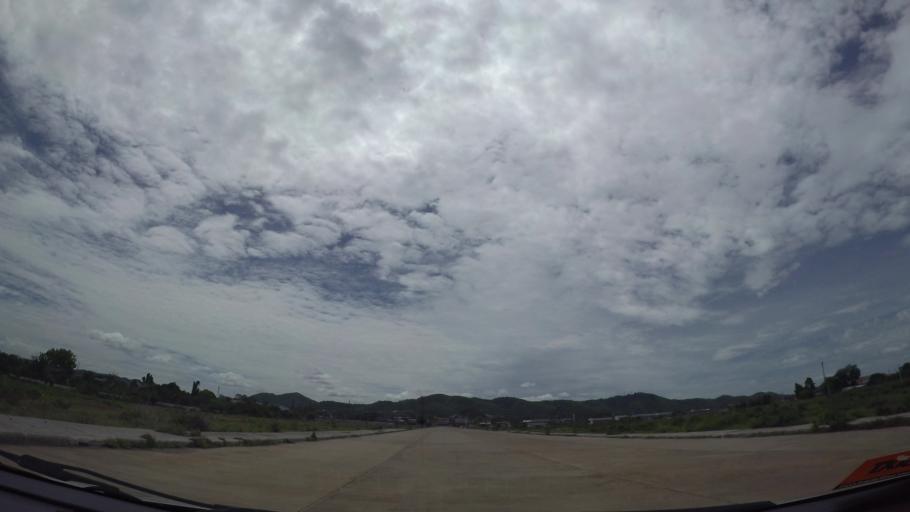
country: TH
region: Chon Buri
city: Sattahip
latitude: 12.6981
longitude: 100.8849
